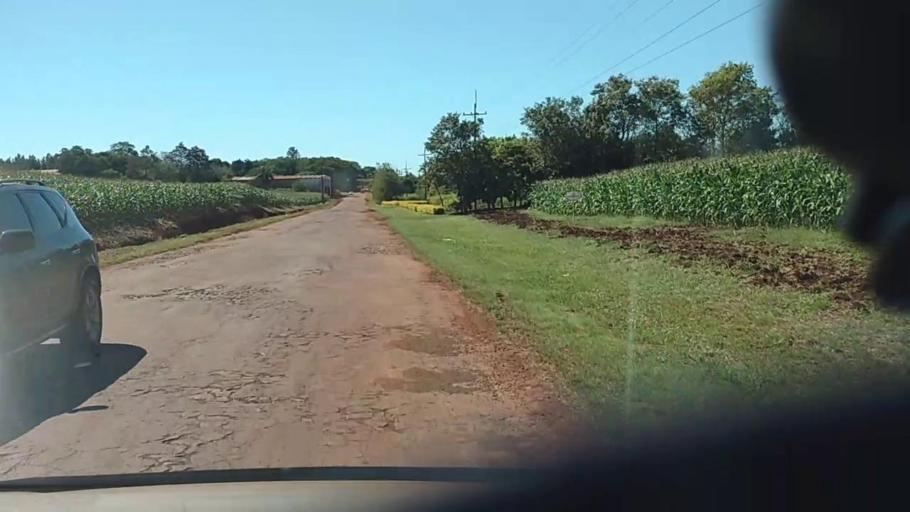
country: PY
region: Alto Parana
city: Naranjal
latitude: -25.9523
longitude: -55.1290
